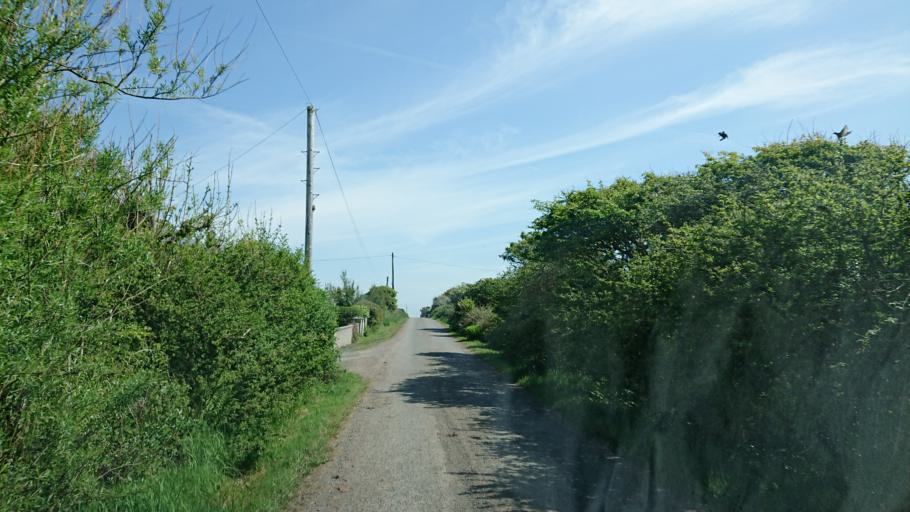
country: IE
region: Munster
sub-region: Waterford
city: Tra Mhor
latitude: 52.1359
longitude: -7.0945
